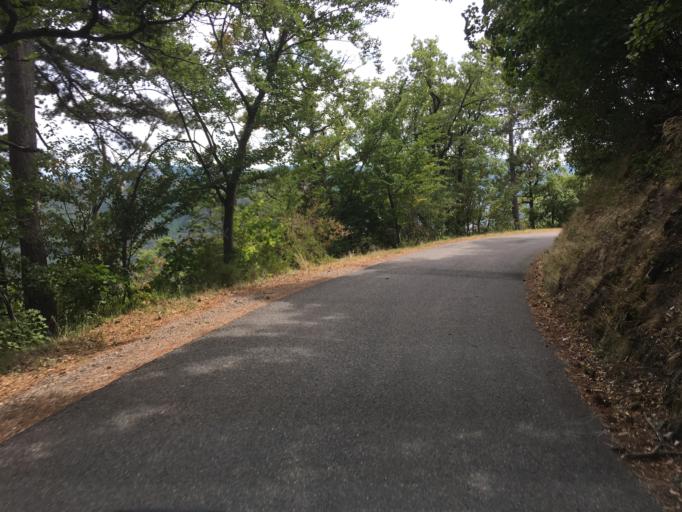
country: FR
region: Provence-Alpes-Cote d'Azur
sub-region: Departement des Alpes-de-Haute-Provence
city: Digne-les-Bains
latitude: 44.2073
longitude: 6.1514
